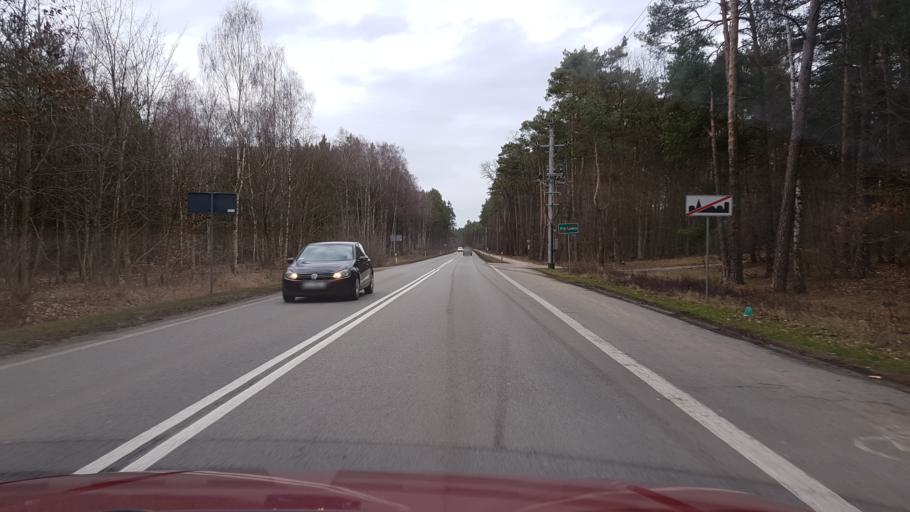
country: PL
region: West Pomeranian Voivodeship
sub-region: Powiat policki
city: Dobra
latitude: 53.5040
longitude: 14.4777
